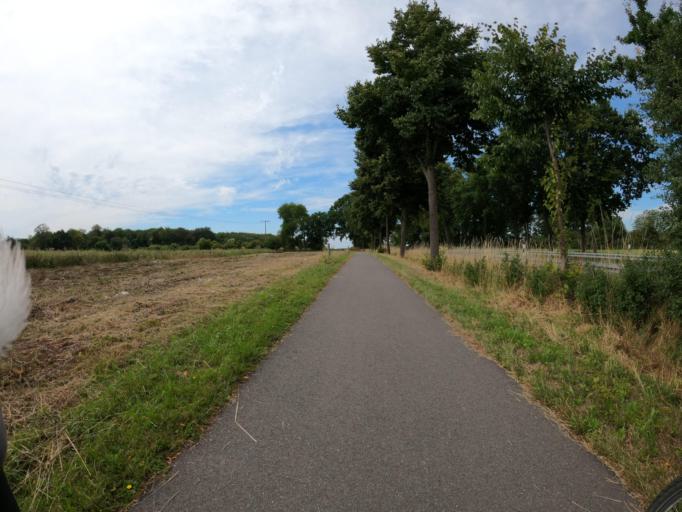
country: DE
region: Mecklenburg-Vorpommern
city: Woldegk
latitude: 53.4507
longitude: 13.5368
